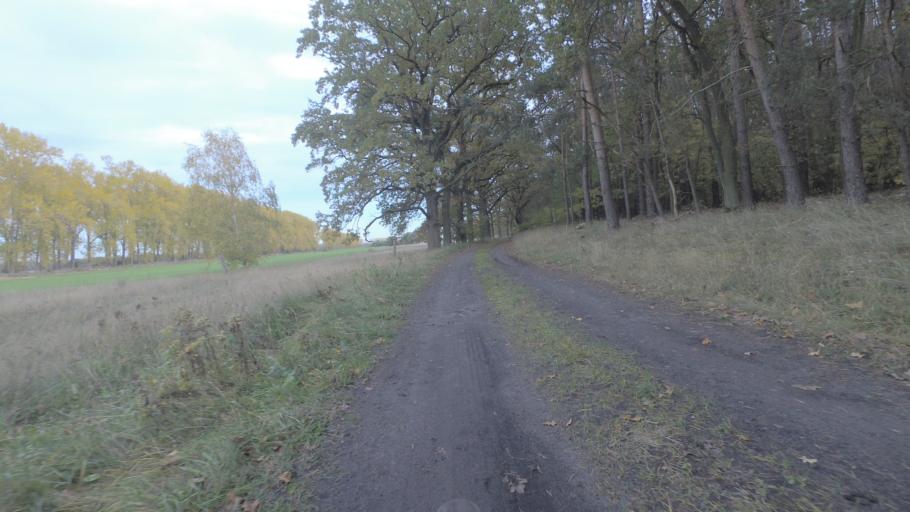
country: DE
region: Brandenburg
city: Ludwigsfelde
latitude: 52.2544
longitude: 13.2753
